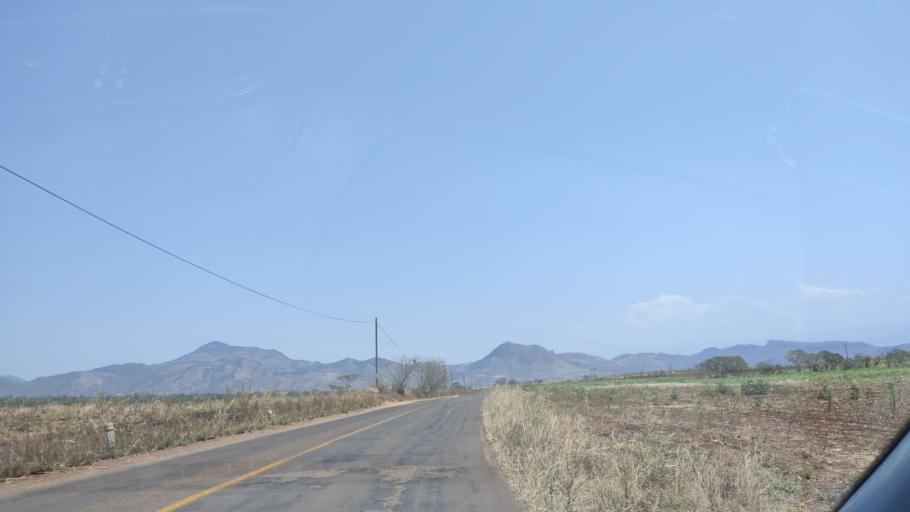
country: MX
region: Nayarit
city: Puga
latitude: 21.5842
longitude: -104.7527
